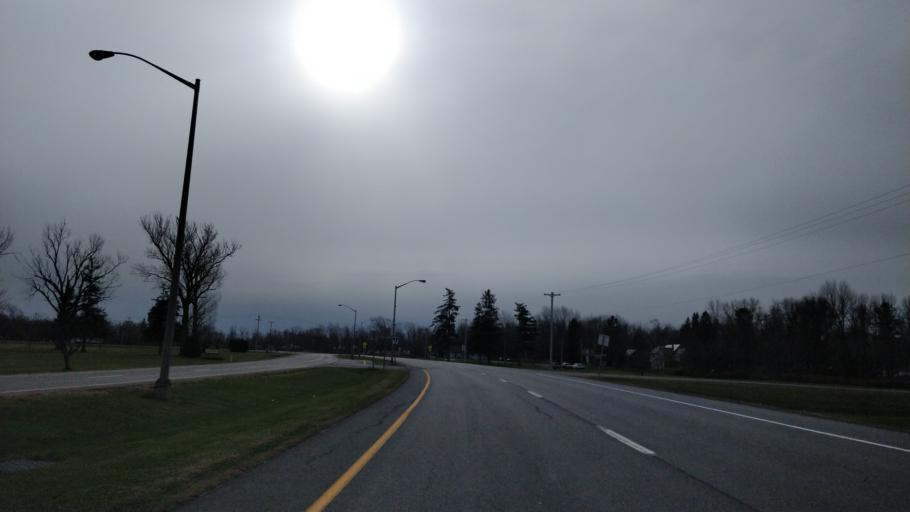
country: US
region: New York
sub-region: St. Lawrence County
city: Ogdensburg
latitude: 44.7176
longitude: -75.4537
